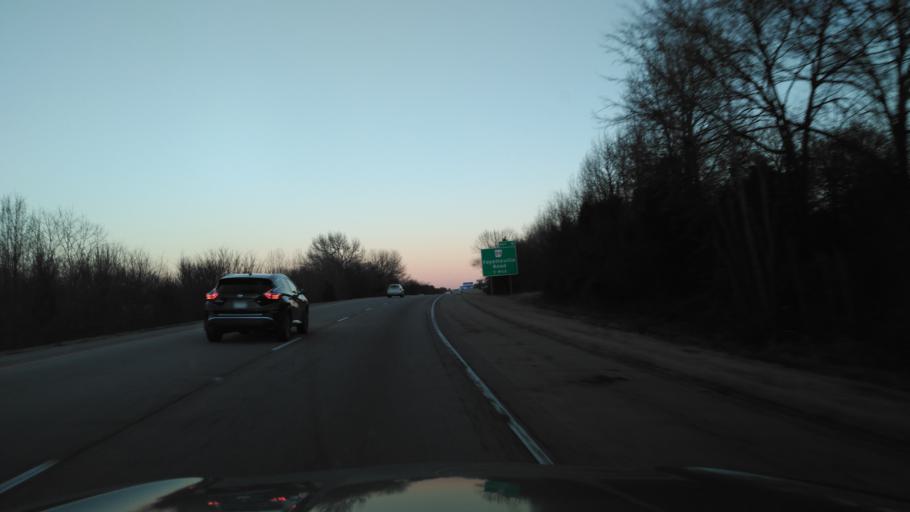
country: US
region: Arkansas
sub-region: Crawford County
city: Van Buren
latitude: 35.4655
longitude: -94.3784
